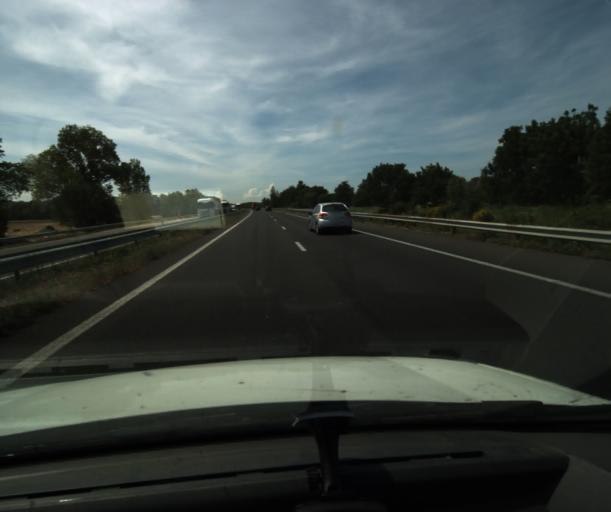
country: FR
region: Languedoc-Roussillon
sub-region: Departement de l'Aude
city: Villeneuve-la-Comptal
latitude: 43.3089
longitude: 1.9063
